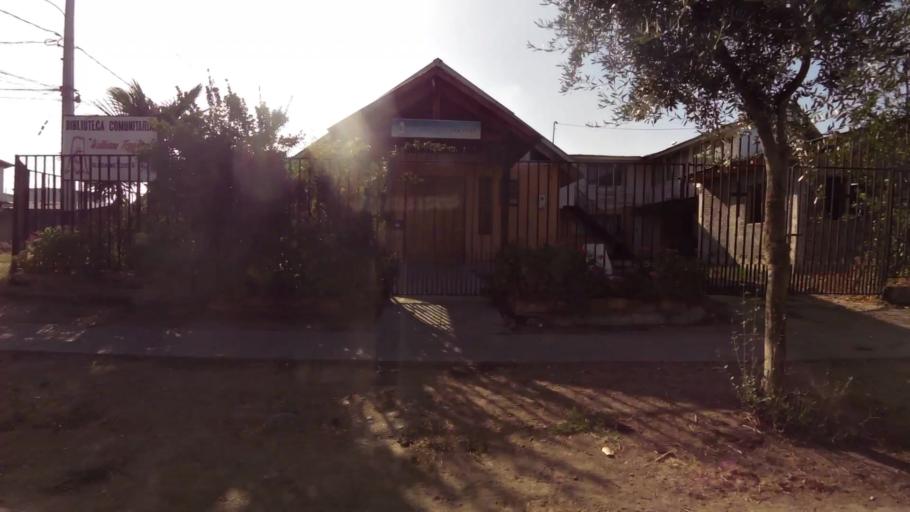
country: CL
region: Maule
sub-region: Provincia de Talca
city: Talca
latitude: -35.4042
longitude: -71.6598
